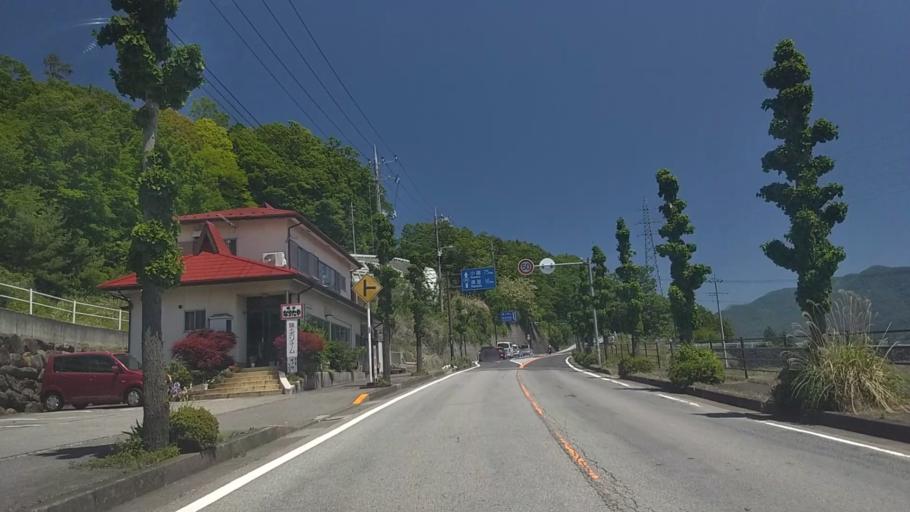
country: JP
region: Yamanashi
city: Nirasaki
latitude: 35.8002
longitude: 138.4251
